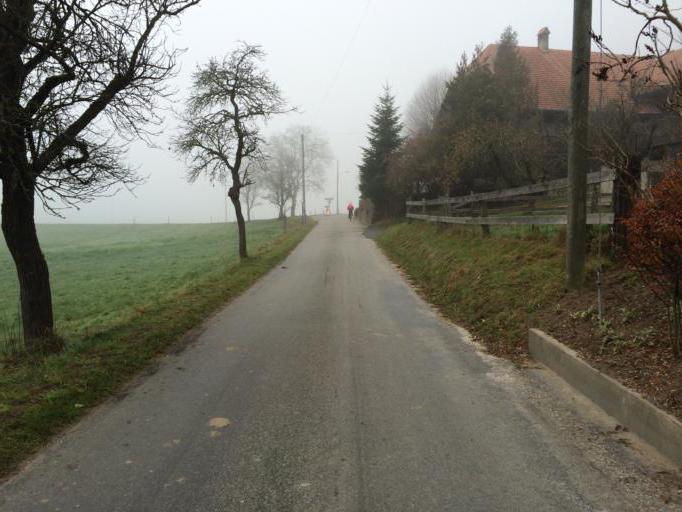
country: CH
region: Bern
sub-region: Bern-Mittelland District
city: Kehrsatz
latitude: 46.9082
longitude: 7.4503
